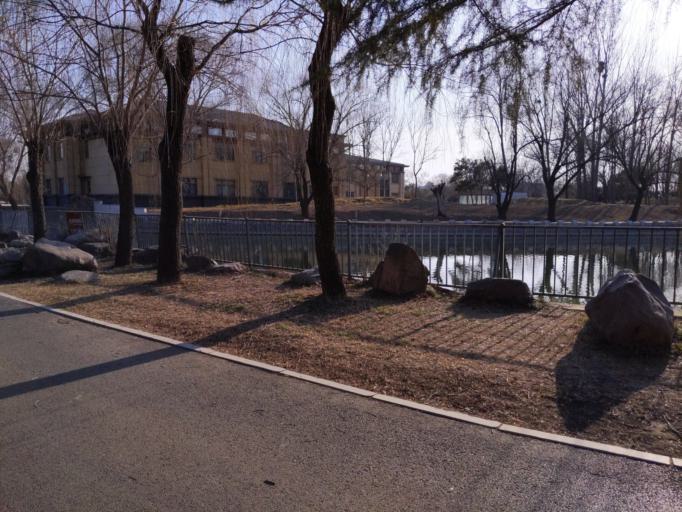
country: CN
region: Henan Sheng
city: Puyang
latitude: 35.7776
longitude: 114.9591
